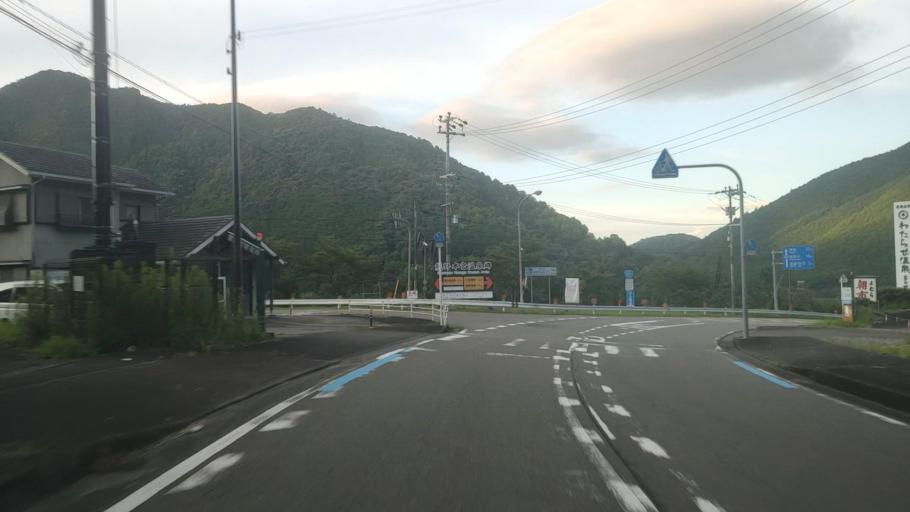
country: JP
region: Wakayama
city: Shingu
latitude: 33.8185
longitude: 135.7607
